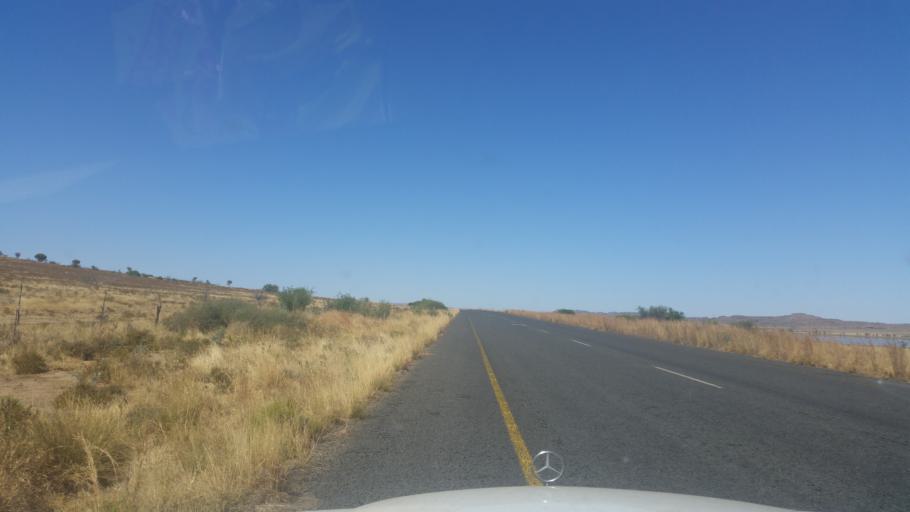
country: ZA
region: Eastern Cape
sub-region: Joe Gqabi District Municipality
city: Burgersdorp
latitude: -30.7076
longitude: 25.8076
